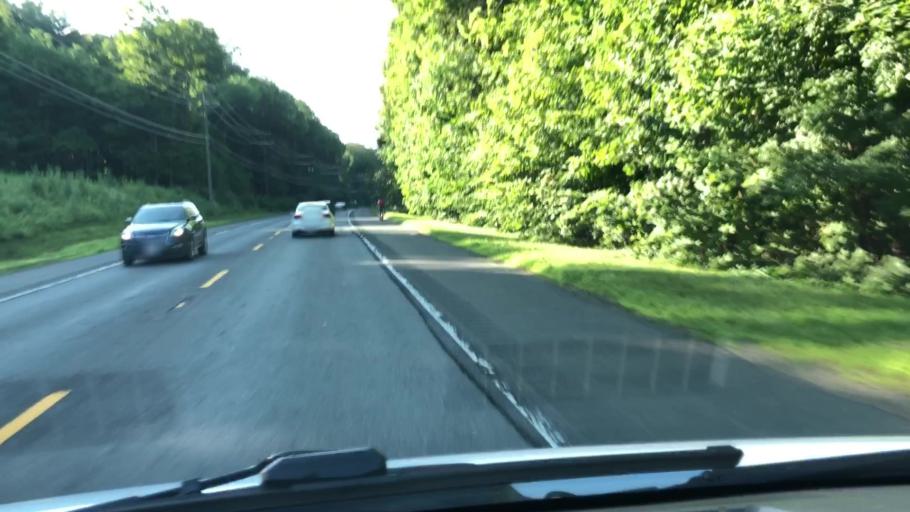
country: US
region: Massachusetts
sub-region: Hampshire County
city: North Amherst
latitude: 42.4416
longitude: -72.5508
